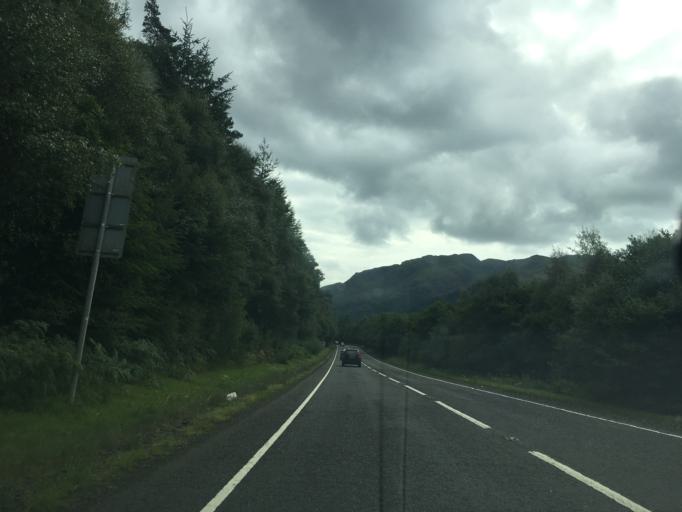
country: GB
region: Scotland
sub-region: Stirling
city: Callander
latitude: 56.3138
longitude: -4.3283
